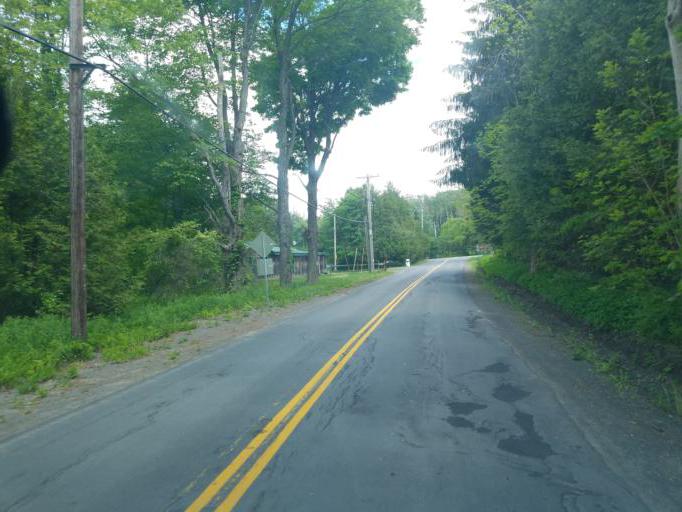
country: US
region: New York
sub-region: Herkimer County
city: Mohawk
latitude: 42.9499
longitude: -75.0153
